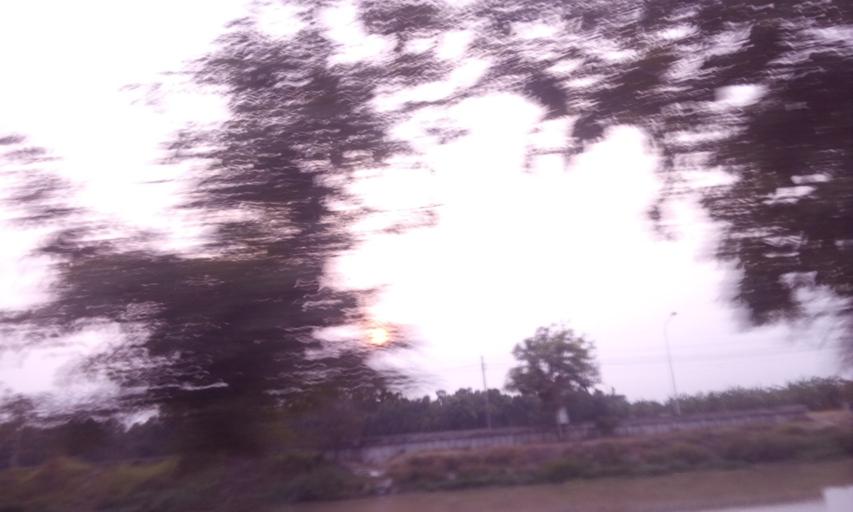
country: TH
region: Bangkok
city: Nong Chok
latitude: 13.9655
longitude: 100.8955
